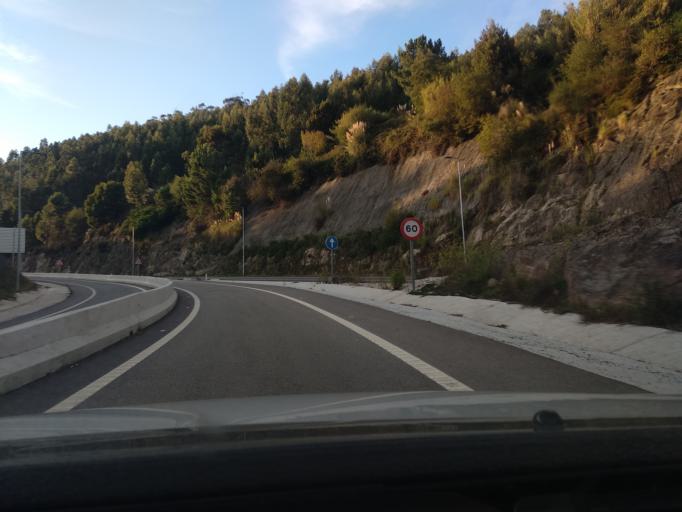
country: ES
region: Galicia
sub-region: Provincia de Pontevedra
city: Redondela
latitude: 42.2922
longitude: -8.6628
